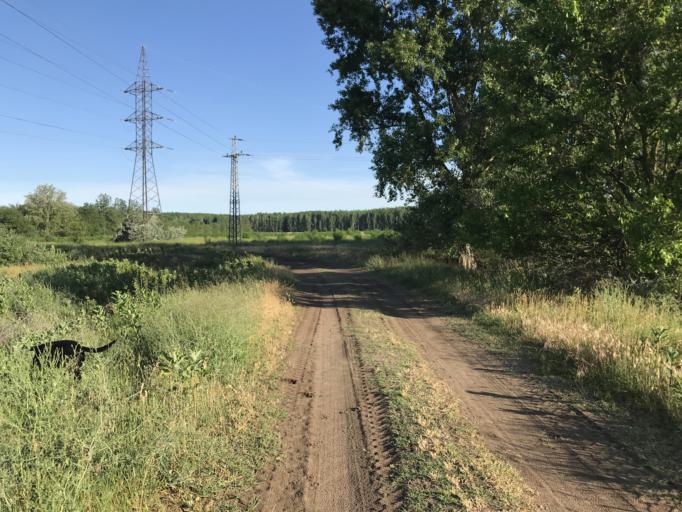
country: HU
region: Bacs-Kiskun
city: Tiszakecske
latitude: 46.9746
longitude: 20.0594
